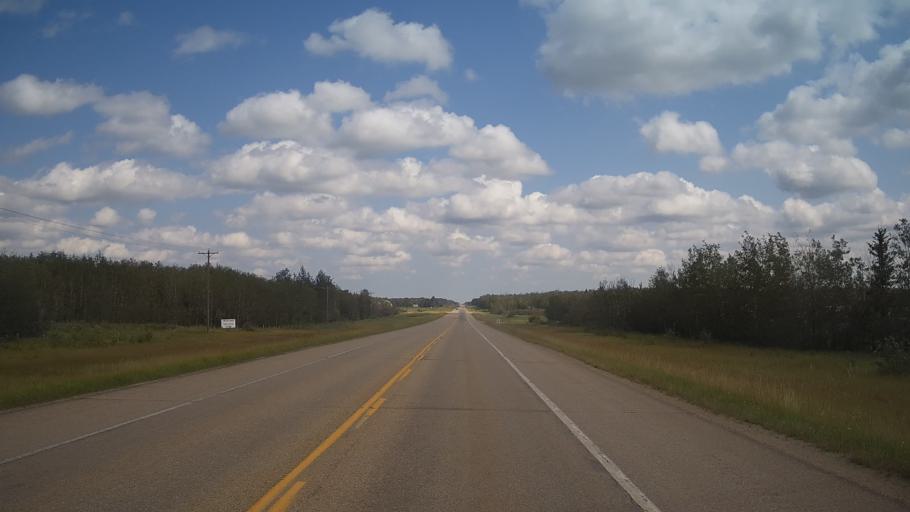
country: CA
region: Alberta
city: Sherwood Park
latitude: 53.3957
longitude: -113.0828
